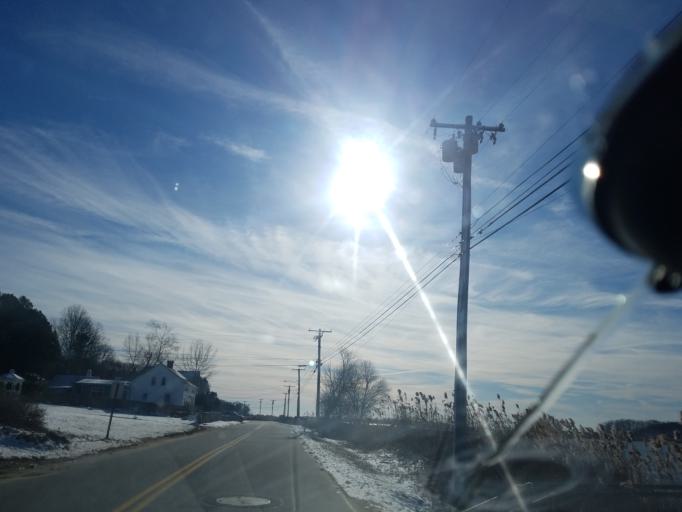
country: US
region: Connecticut
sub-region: New London County
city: Niantic
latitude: 41.3049
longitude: -72.2175
